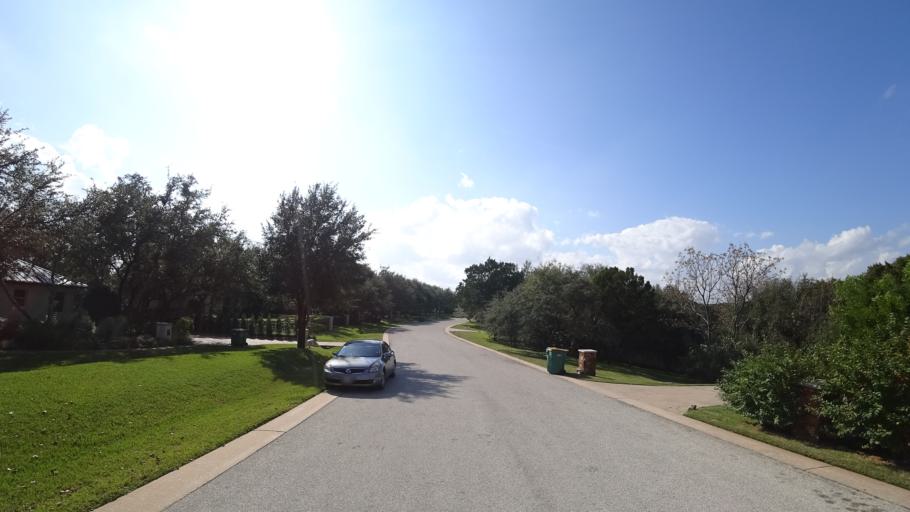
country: US
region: Texas
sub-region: Travis County
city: Lost Creek
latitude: 30.3078
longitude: -97.8570
